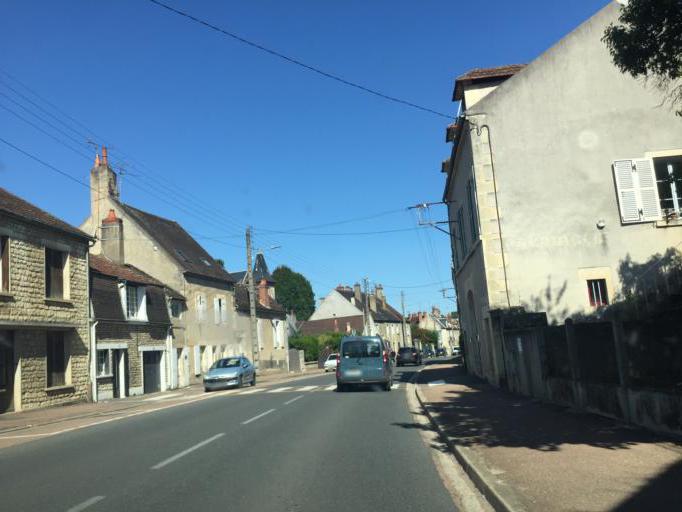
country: FR
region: Bourgogne
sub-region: Departement de la Nievre
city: Clamecy
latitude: 47.4572
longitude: 3.5267
